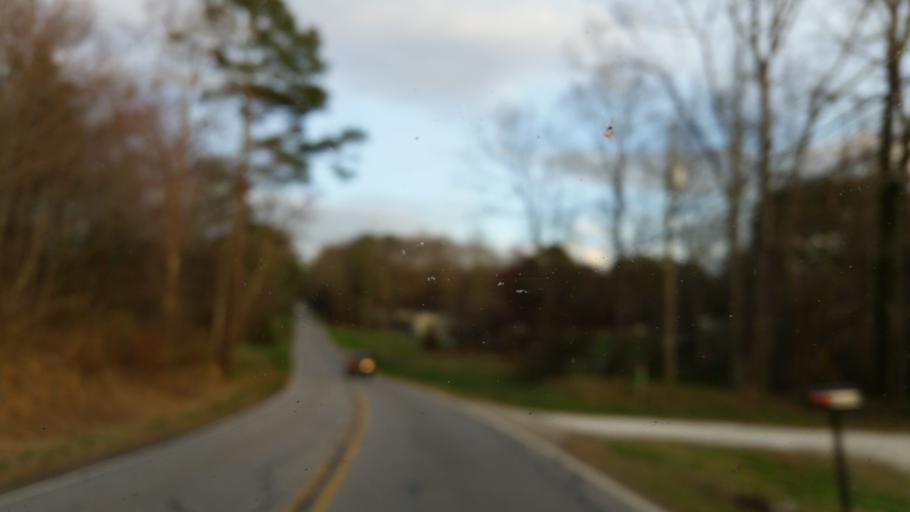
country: US
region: Georgia
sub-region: Pickens County
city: Jasper
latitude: 34.4773
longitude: -84.5753
